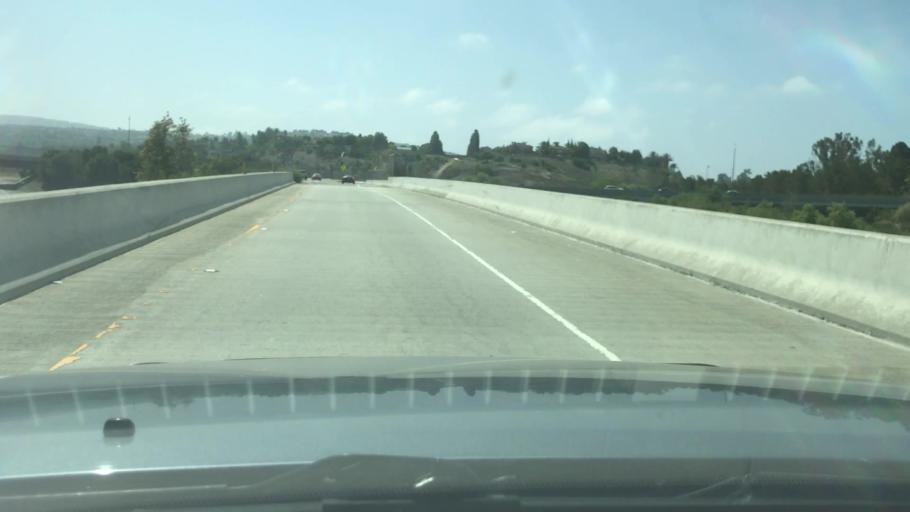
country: US
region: California
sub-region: Orange County
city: San Joaquin Hills
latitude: 33.6392
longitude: -117.8586
